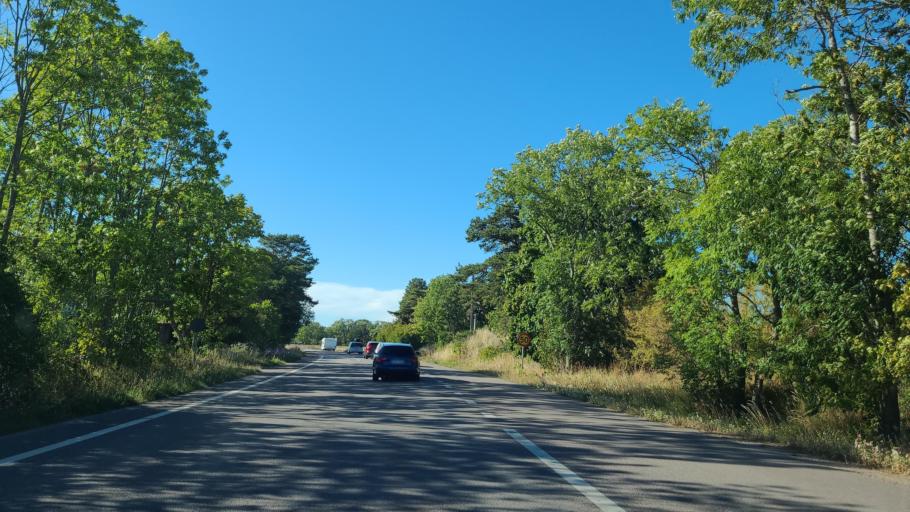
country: SE
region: Kalmar
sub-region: Borgholms Kommun
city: Borgholm
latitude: 57.2506
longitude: 17.0568
